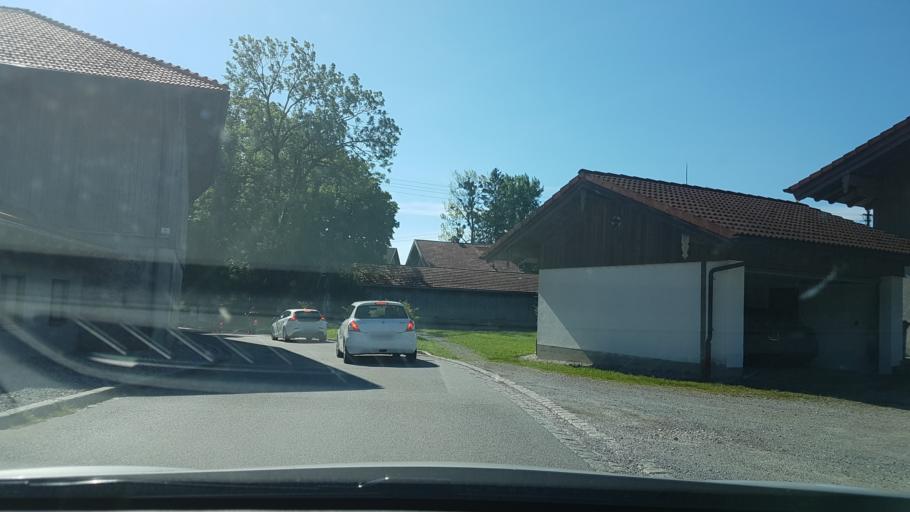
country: DE
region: Bavaria
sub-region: Upper Bavaria
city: Valley
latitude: 47.8903
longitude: 11.7682
